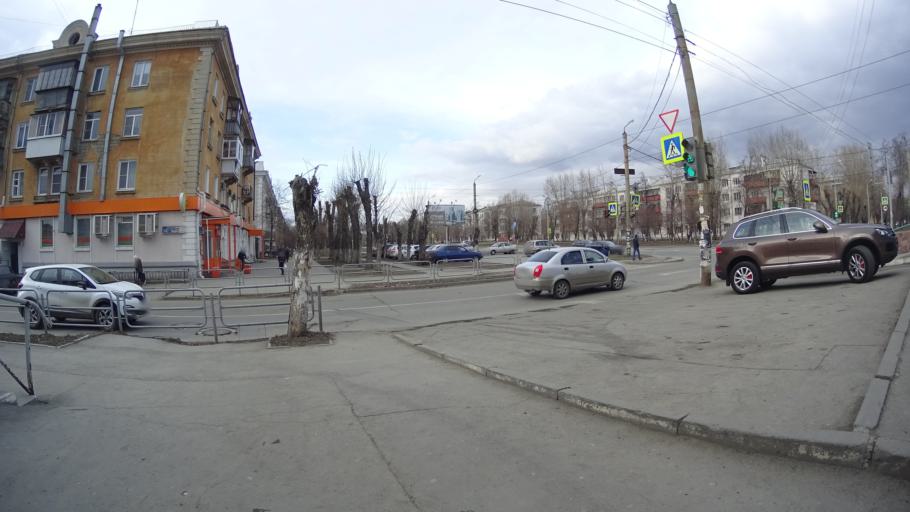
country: RU
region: Chelyabinsk
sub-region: Gorod Chelyabinsk
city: Chelyabinsk
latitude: 55.1620
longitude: 61.4410
